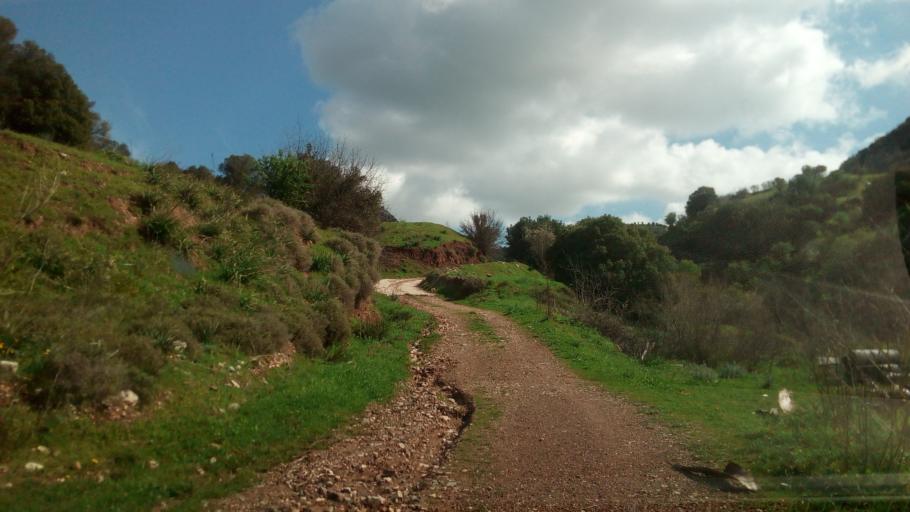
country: CY
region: Pafos
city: Mesogi
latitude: 34.8054
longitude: 32.5371
